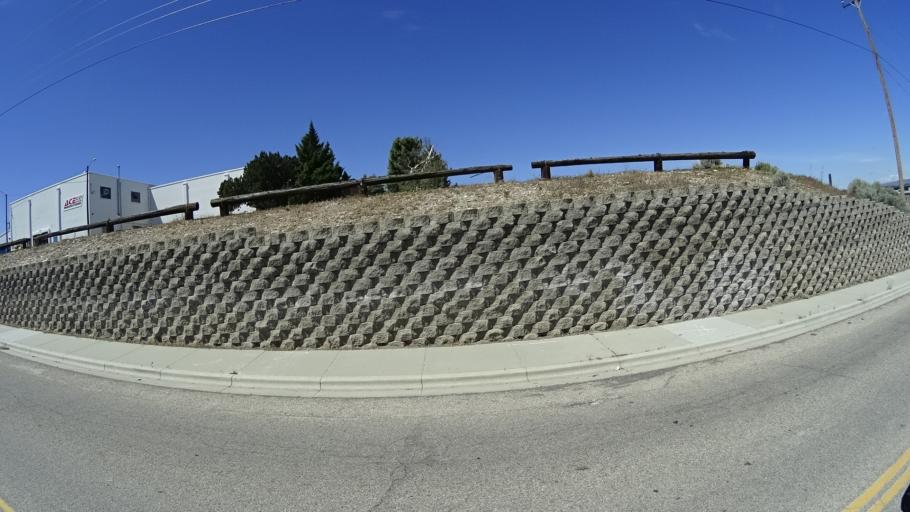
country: US
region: Idaho
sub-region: Ada County
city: Boise
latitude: 43.5652
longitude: -116.1834
